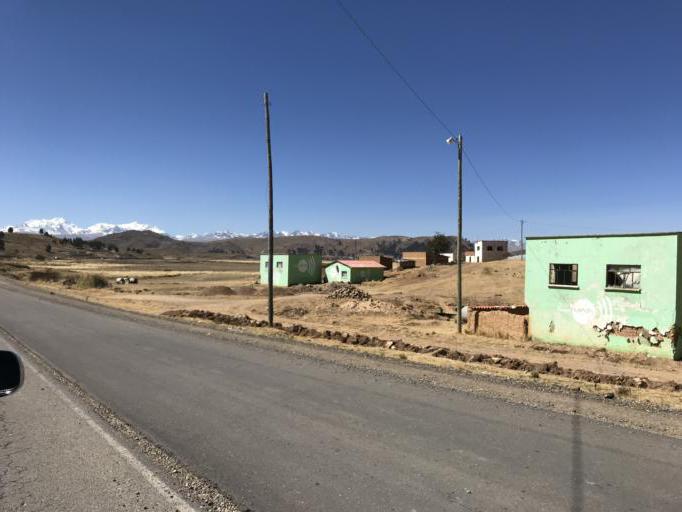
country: BO
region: La Paz
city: Huarina
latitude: -16.2023
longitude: -68.6325
